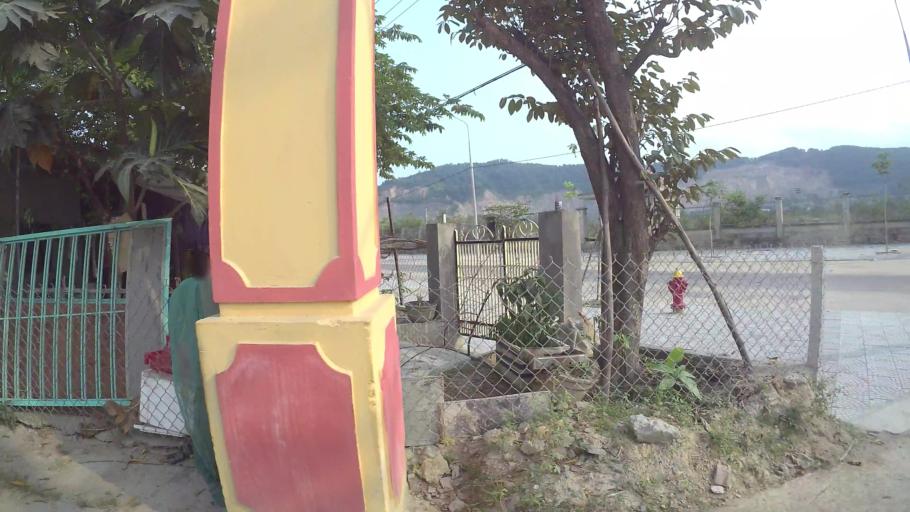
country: VN
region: Da Nang
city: Lien Chieu
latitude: 16.0478
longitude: 108.1568
